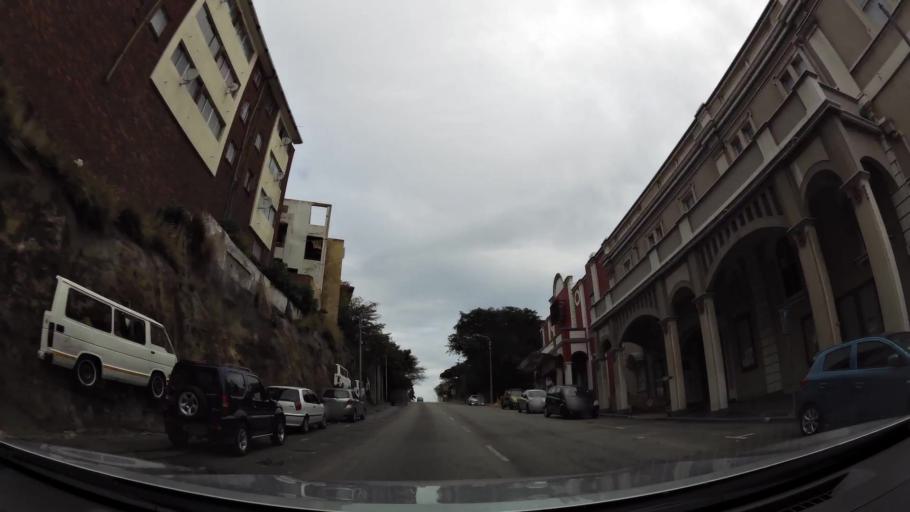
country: ZA
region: Eastern Cape
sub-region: Nelson Mandela Bay Metropolitan Municipality
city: Port Elizabeth
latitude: -33.9625
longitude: 25.6219
